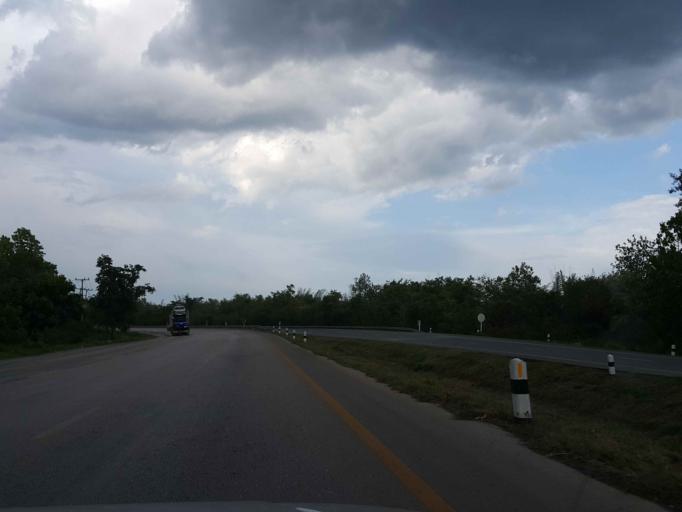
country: TH
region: Lampang
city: Sop Prap
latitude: 17.9718
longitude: 99.3541
